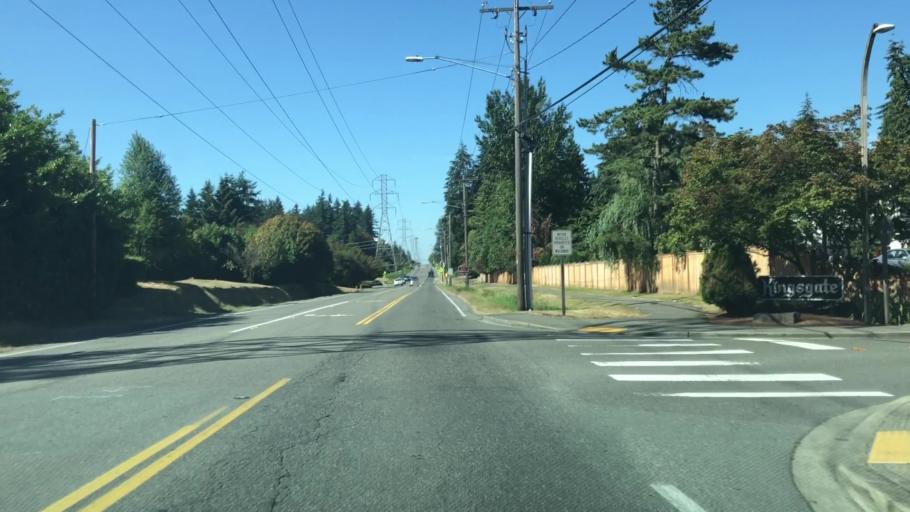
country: US
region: Washington
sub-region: King County
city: Kingsgate
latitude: 47.7343
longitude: -122.1755
